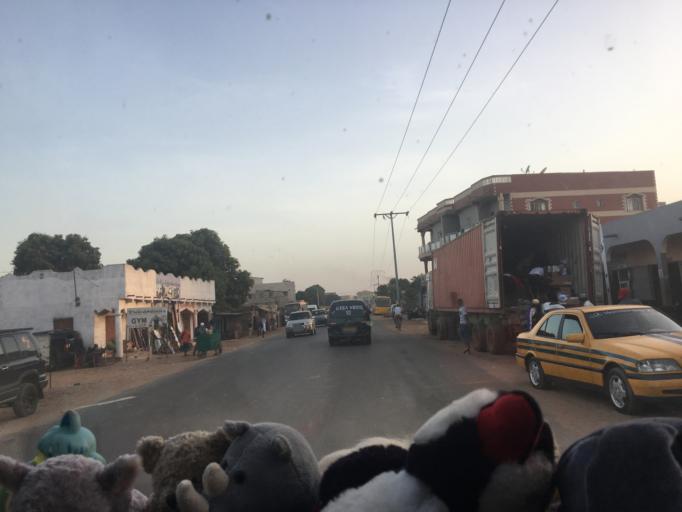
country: GM
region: Western
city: Abuko
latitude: 13.3878
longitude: -16.6765
